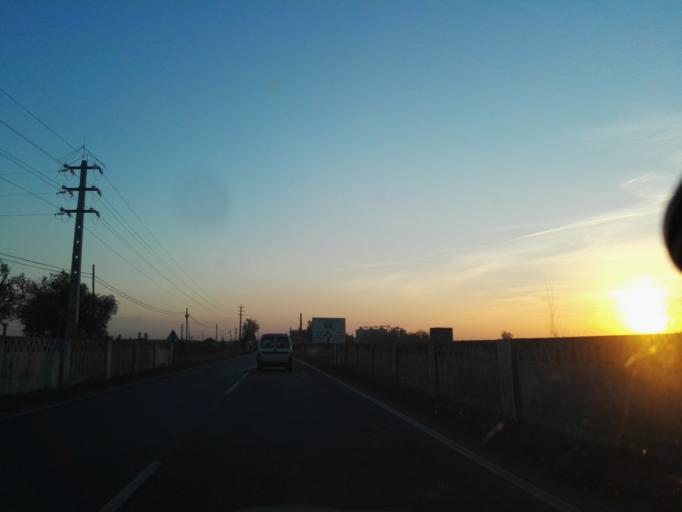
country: PT
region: Santarem
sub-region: Coruche
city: Coruche
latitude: 38.9504
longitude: -8.4967
